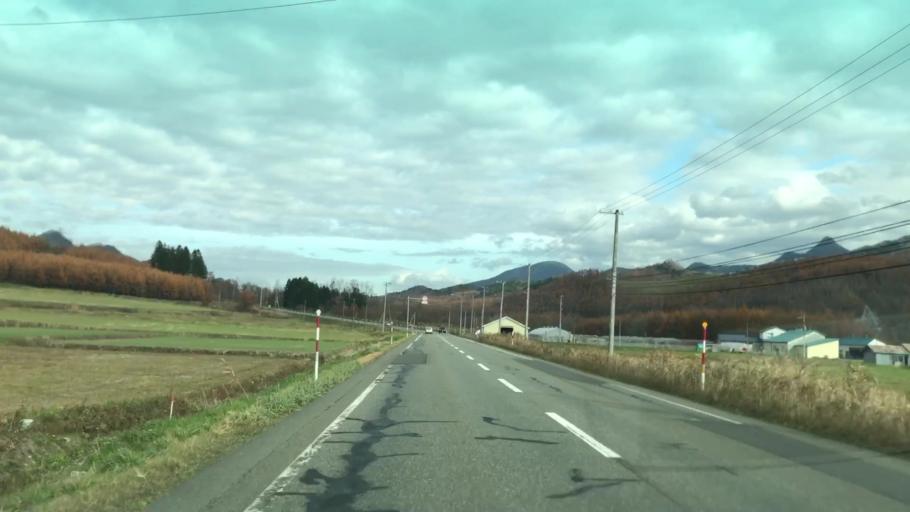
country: JP
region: Hokkaido
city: Shizunai-furukawacho
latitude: 42.7403
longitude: 142.3602
